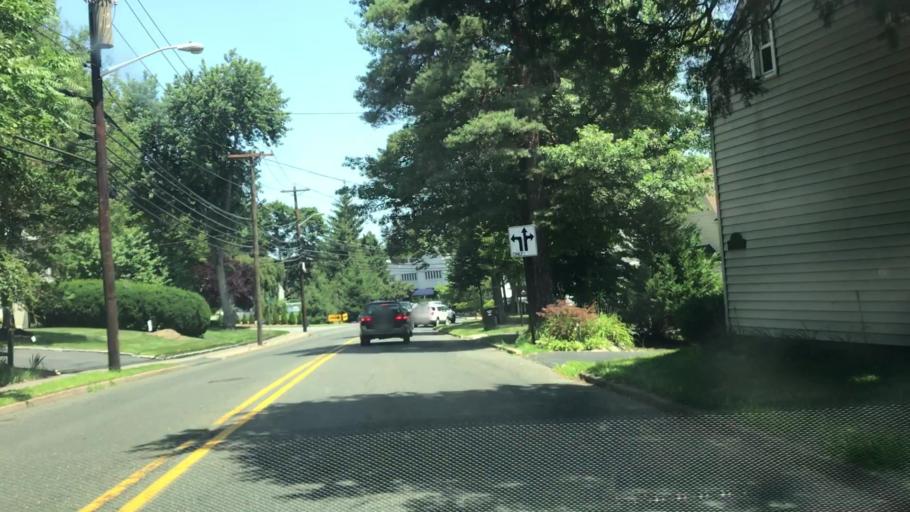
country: US
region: New Jersey
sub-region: Bergen County
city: River Edge
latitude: 40.9343
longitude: -74.0530
